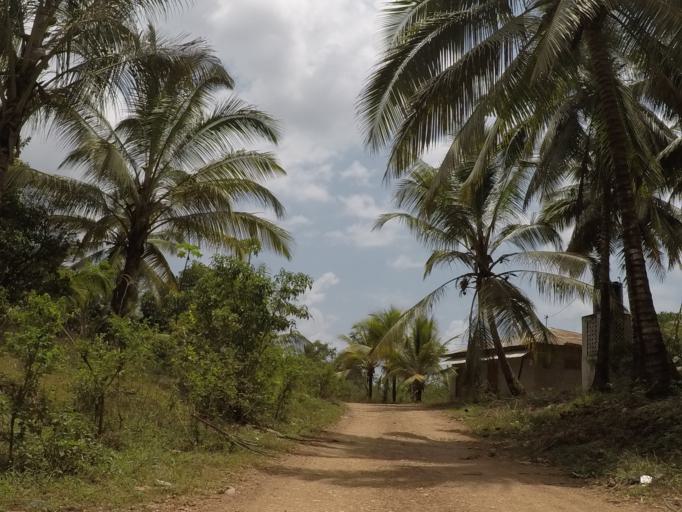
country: TZ
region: Zanzibar Central/South
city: Koani
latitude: -6.1920
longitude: 39.3070
